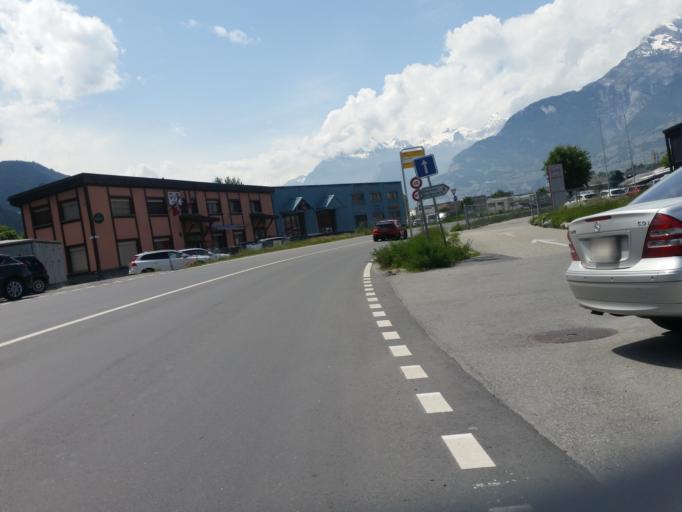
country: CH
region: Valais
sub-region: Sion District
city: Sitten
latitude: 46.2186
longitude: 7.3492
